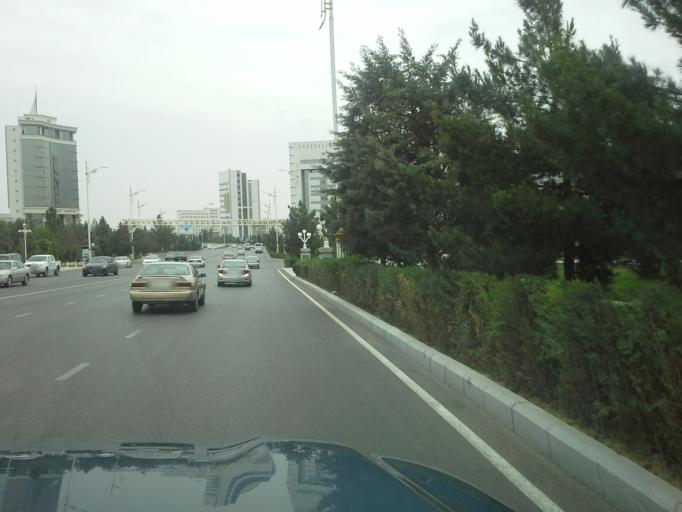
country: TM
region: Ahal
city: Ashgabat
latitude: 37.9265
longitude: 58.3732
